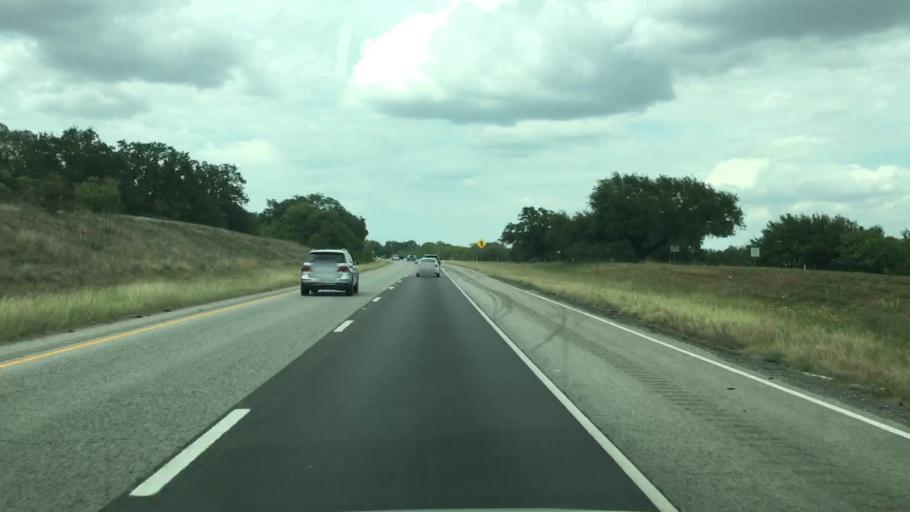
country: US
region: Texas
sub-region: Atascosa County
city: Pleasanton
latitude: 29.0359
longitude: -98.4321
